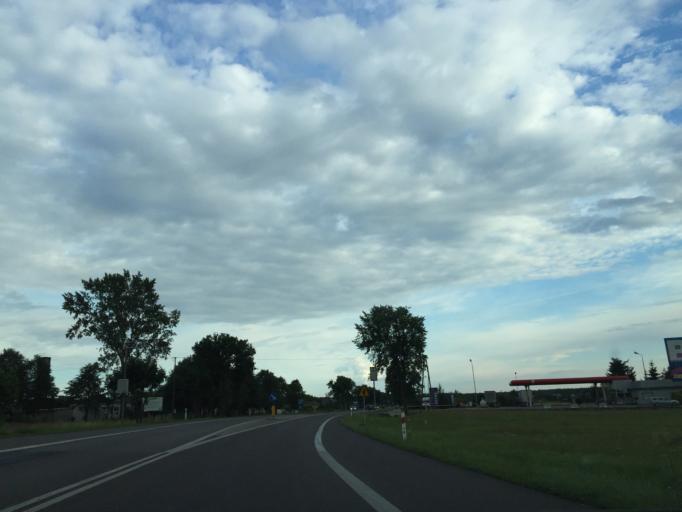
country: PL
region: Lublin Voivodeship
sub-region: Powiat lubartowski
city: Firlej
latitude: 51.5658
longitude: 22.5031
